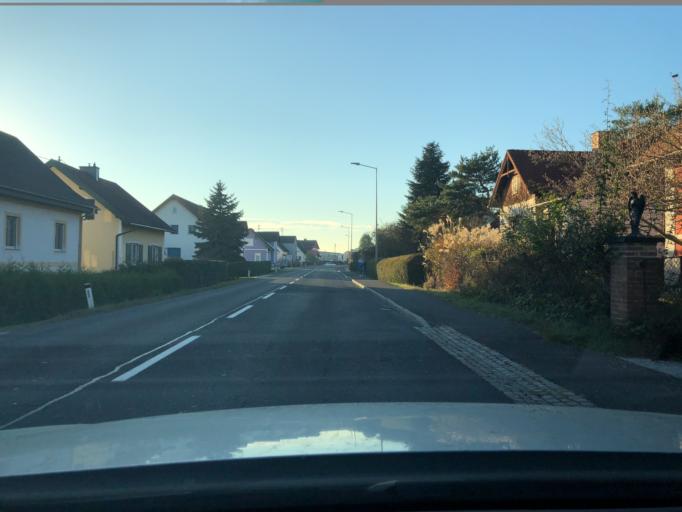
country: AT
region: Styria
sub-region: Politischer Bezirk Hartberg-Fuerstenfeld
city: Ilz
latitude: 47.0871
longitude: 15.9211
